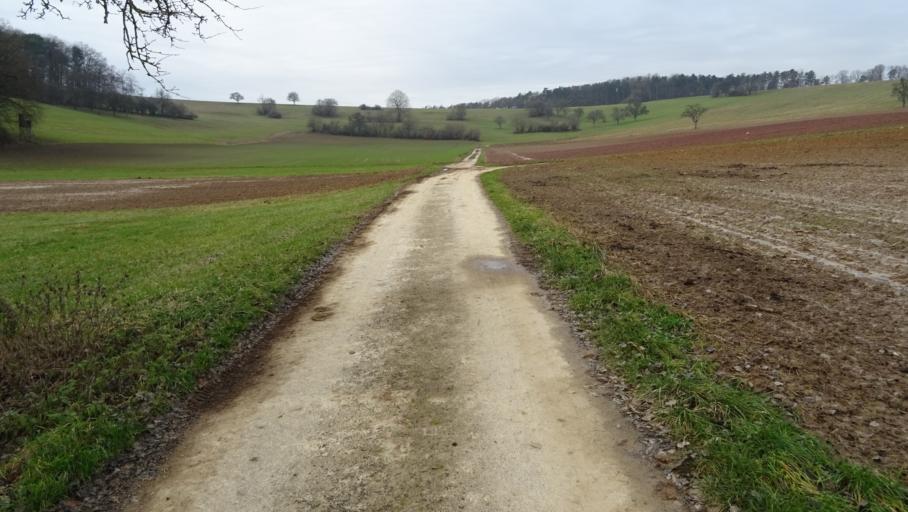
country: DE
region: Baden-Wuerttemberg
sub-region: Karlsruhe Region
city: Mosbach
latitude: 49.3600
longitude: 9.1815
